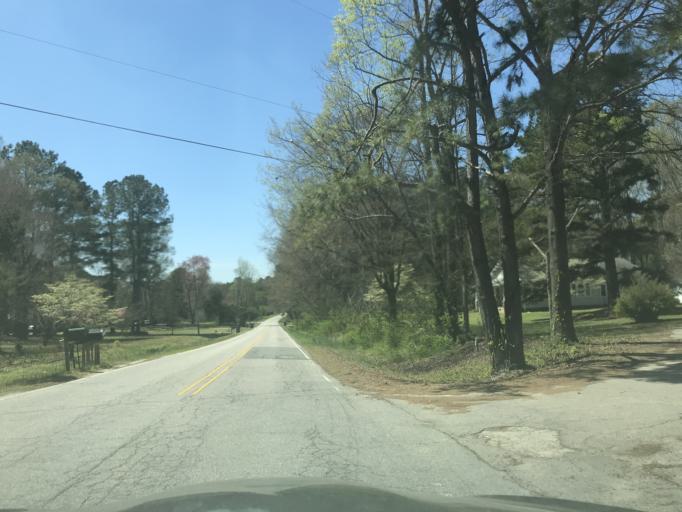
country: US
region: North Carolina
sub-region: Wake County
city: Knightdale
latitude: 35.8481
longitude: -78.5567
